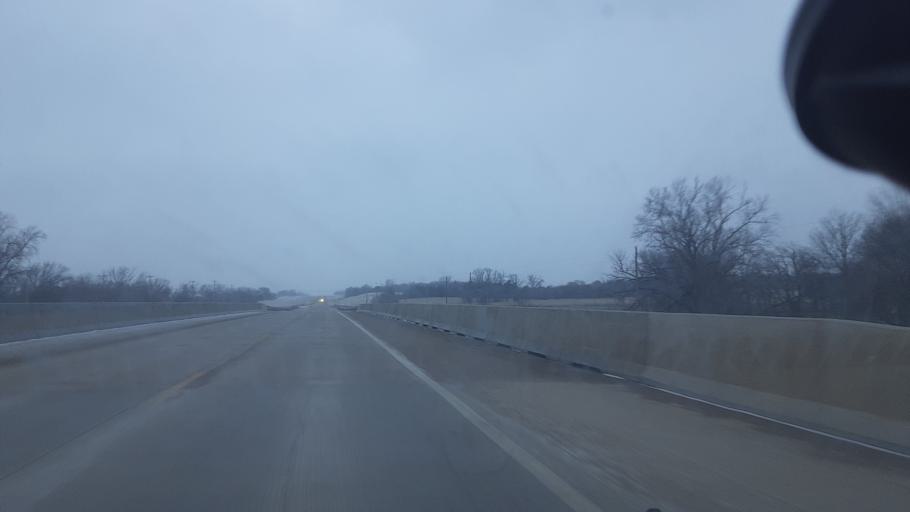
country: US
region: Oklahoma
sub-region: Payne County
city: Perkins
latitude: 35.9859
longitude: -97.1184
